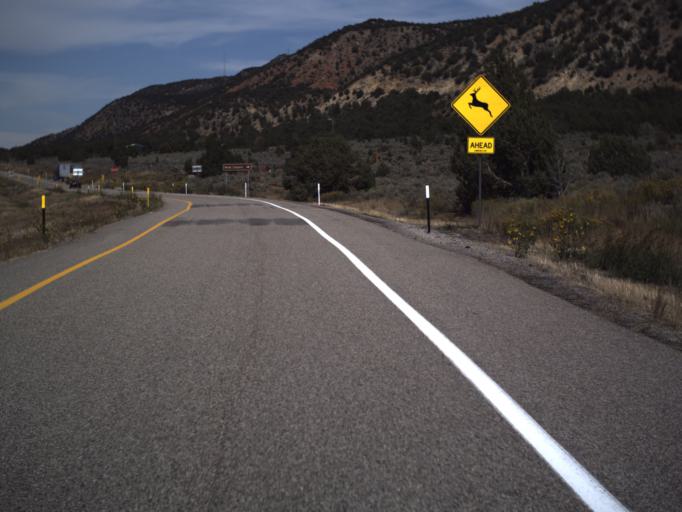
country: US
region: Utah
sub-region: Washington County
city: Toquerville
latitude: 37.4524
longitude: -113.2283
